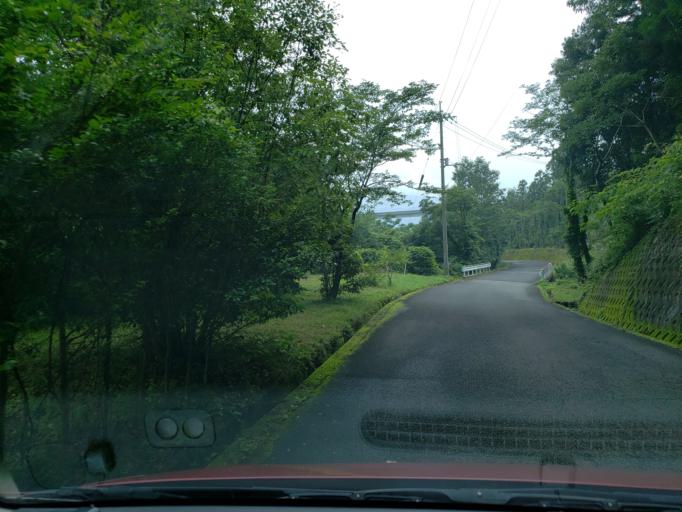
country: JP
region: Tokushima
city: Kamojimacho-jogejima
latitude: 34.1069
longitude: 134.2981
